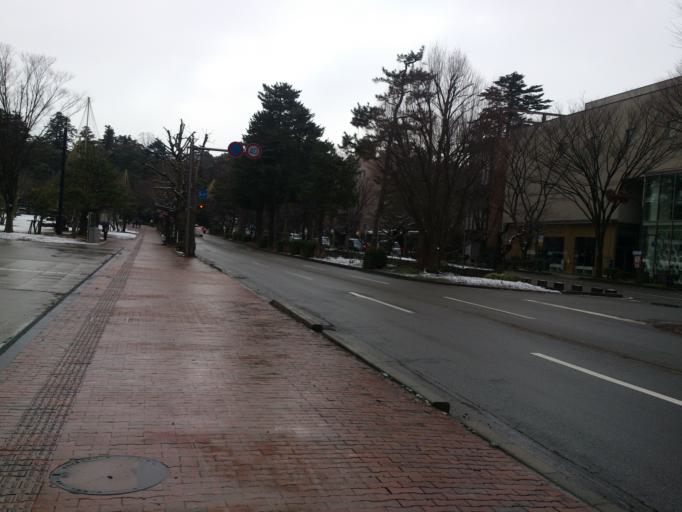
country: JP
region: Ishikawa
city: Kanazawa-shi
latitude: 36.5620
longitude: 136.6576
